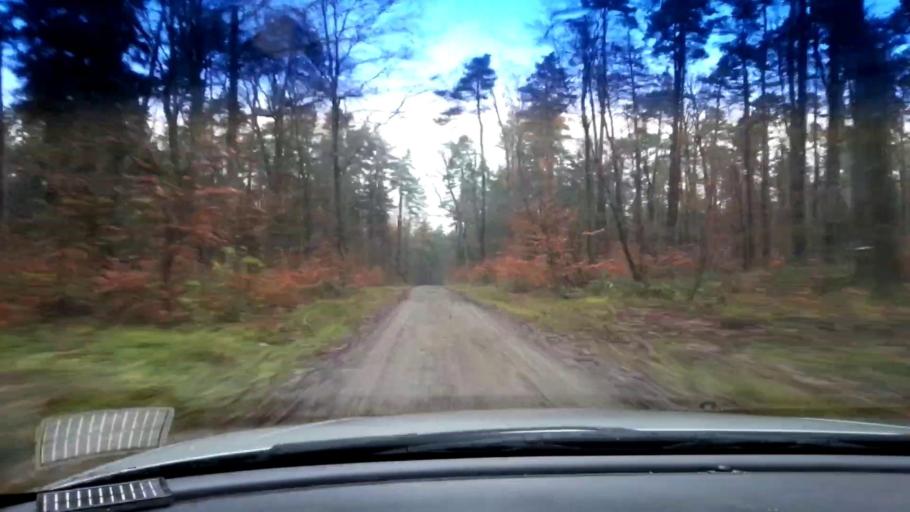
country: DE
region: Bavaria
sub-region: Upper Franconia
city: Gundelsheim
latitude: 49.9469
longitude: 10.9334
